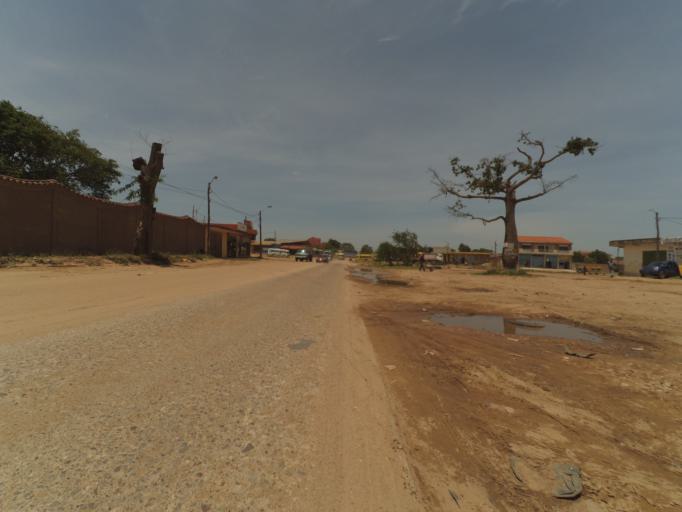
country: BO
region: Santa Cruz
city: Santa Cruz de la Sierra
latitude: -17.8311
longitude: -63.2411
